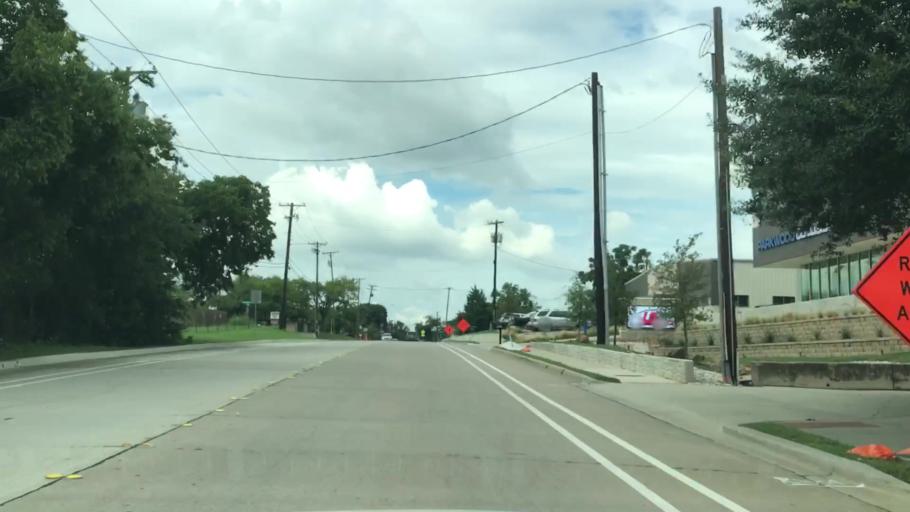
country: US
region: Texas
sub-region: Collin County
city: Frisco
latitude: 33.1449
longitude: -96.8253
